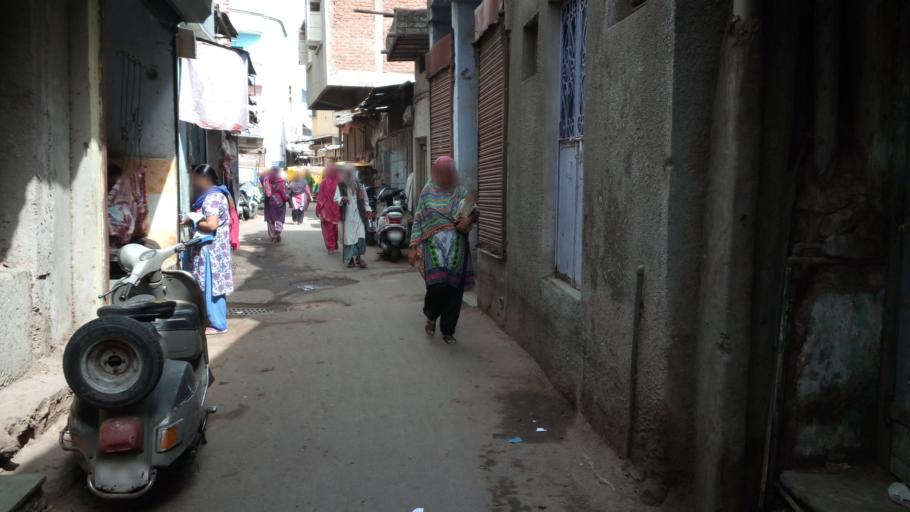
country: IN
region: Gujarat
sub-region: Ahmadabad
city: Ahmedabad
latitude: 23.0138
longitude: 72.5823
